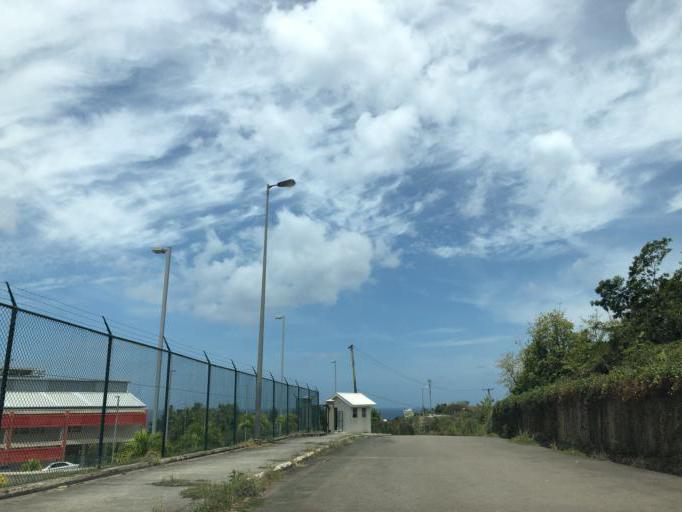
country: LC
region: Castries Quarter
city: Castries
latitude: 14.0019
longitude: -61.0090
